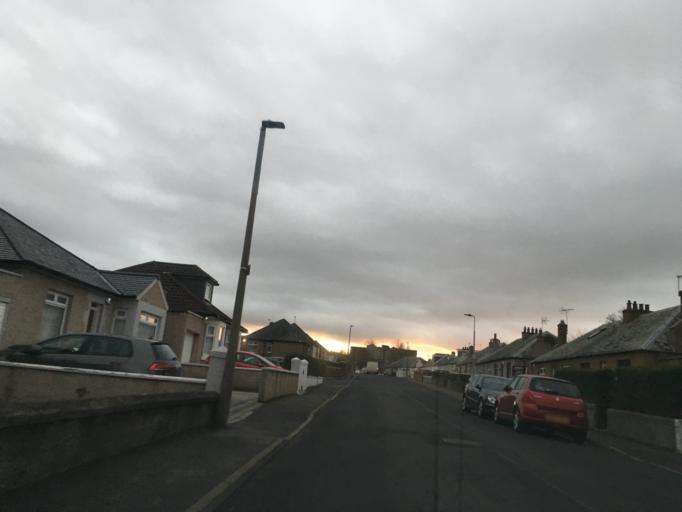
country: GB
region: Scotland
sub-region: Edinburgh
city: Colinton
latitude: 55.9213
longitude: -3.2639
